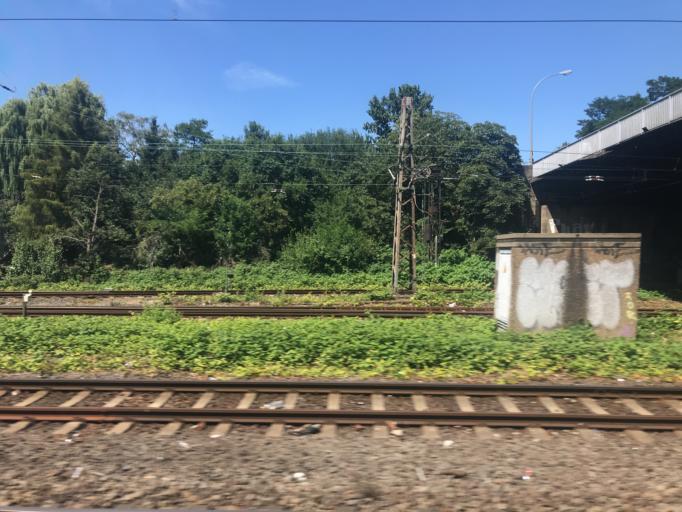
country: DE
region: North Rhine-Westphalia
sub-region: Regierungsbezirk Arnsberg
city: Dortmund
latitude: 51.5215
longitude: 7.4876
